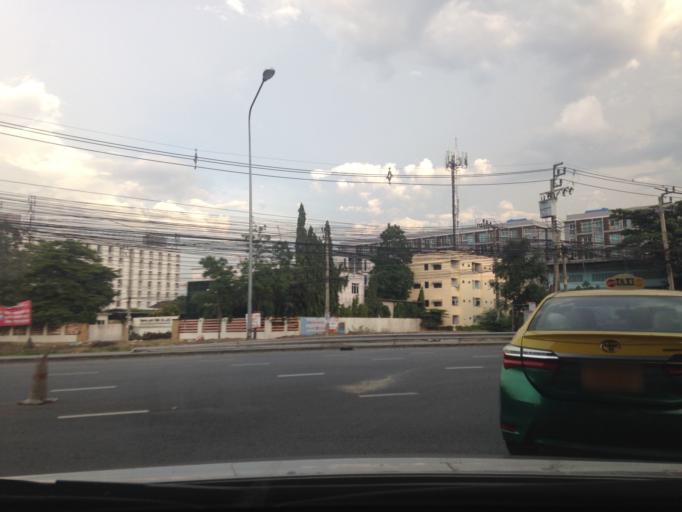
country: TH
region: Bangkok
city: Khan Na Yao
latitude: 13.8289
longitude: 100.6746
